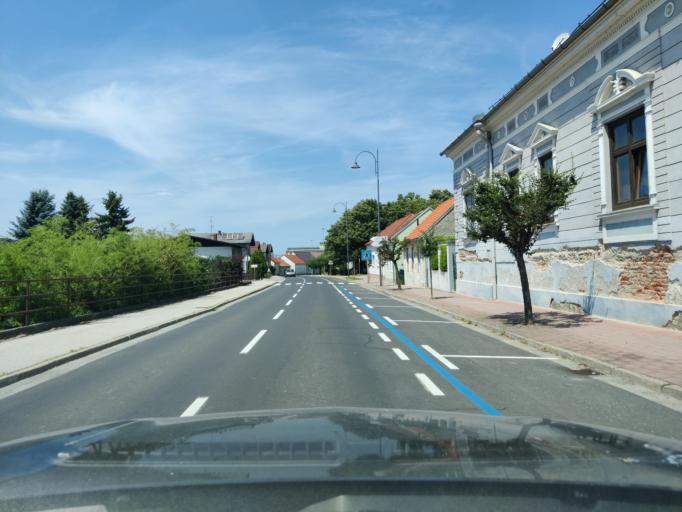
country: SI
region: Lendava-Lendva
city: Lendava
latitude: 46.5685
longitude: 16.4498
